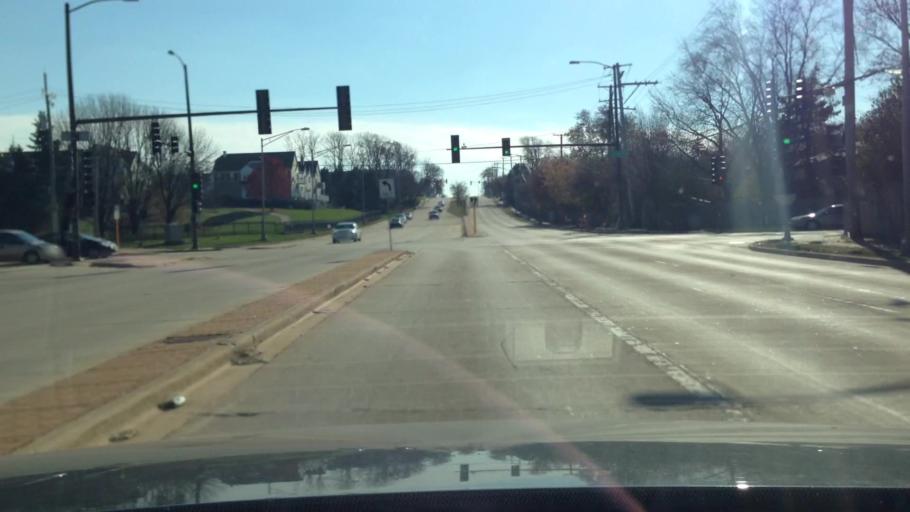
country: US
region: Illinois
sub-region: DuPage County
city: Downers Grove
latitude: 41.8451
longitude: -88.0263
